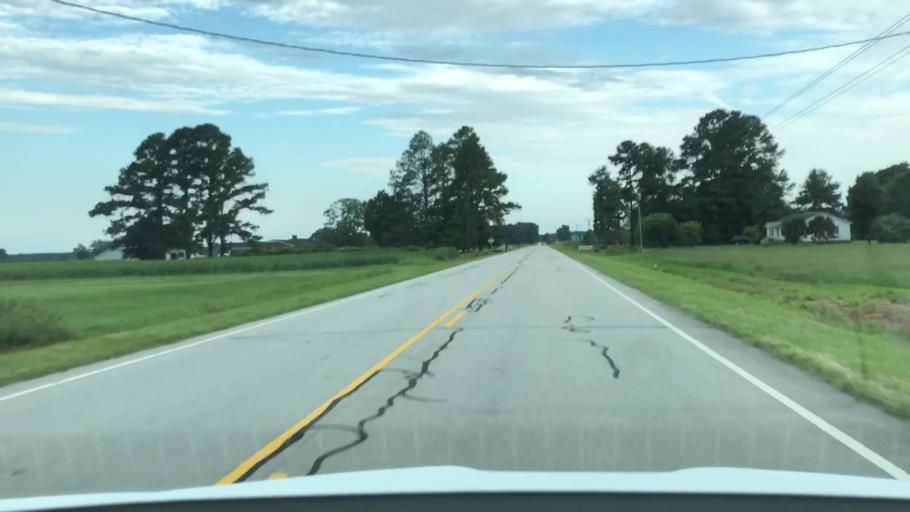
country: US
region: North Carolina
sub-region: Jones County
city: Trenton
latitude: 35.0974
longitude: -77.4833
